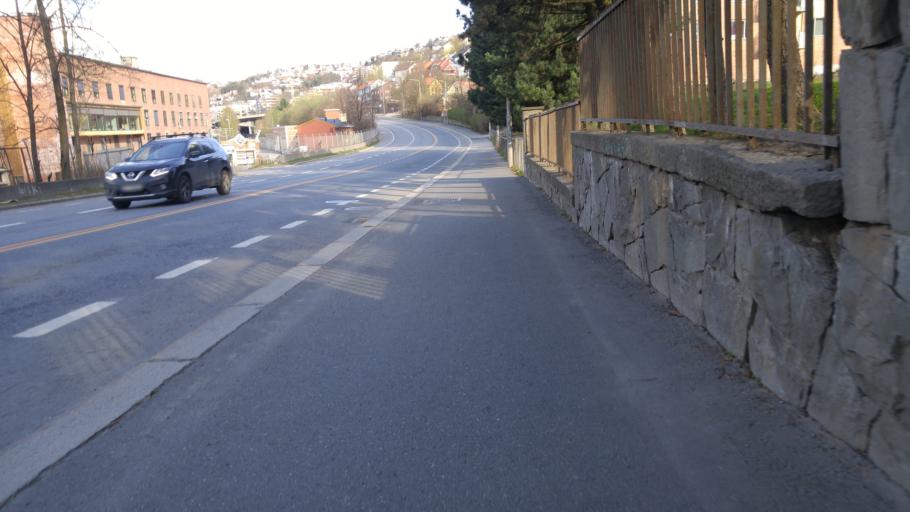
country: NO
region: Oslo
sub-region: Oslo
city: Oslo
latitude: 59.9041
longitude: 10.7738
